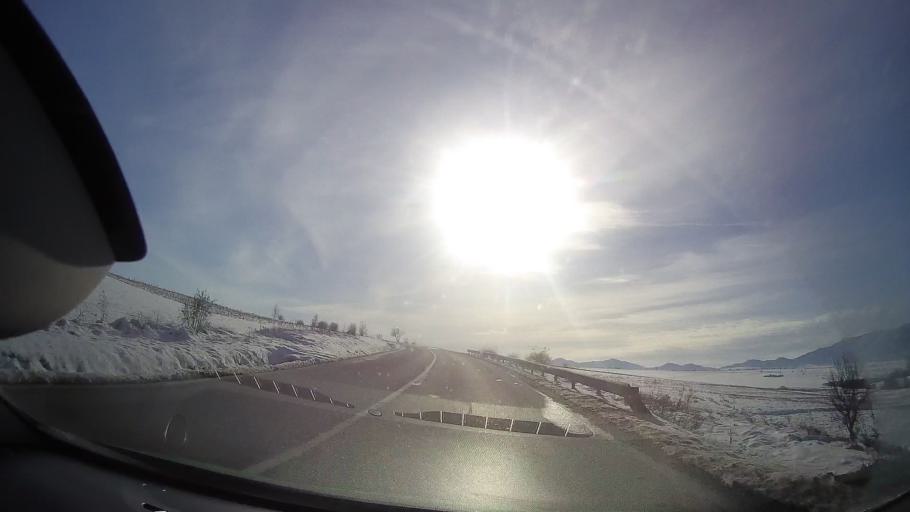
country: RO
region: Neamt
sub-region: Comuna Baltatesti
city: Valea Seaca
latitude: 47.1640
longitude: 26.3181
